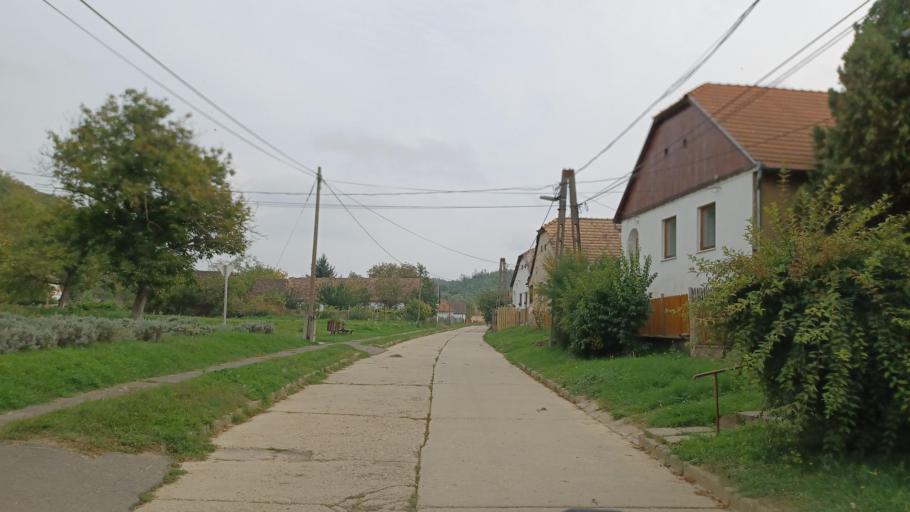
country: HU
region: Tolna
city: Gyonk
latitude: 46.5715
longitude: 18.4266
